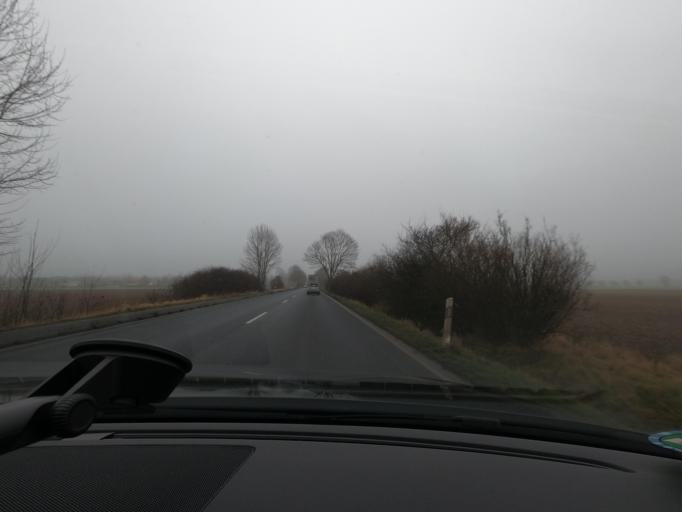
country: DE
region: North Rhine-Westphalia
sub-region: Regierungsbezirk Koln
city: Merzenich
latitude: 50.8169
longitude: 6.5261
